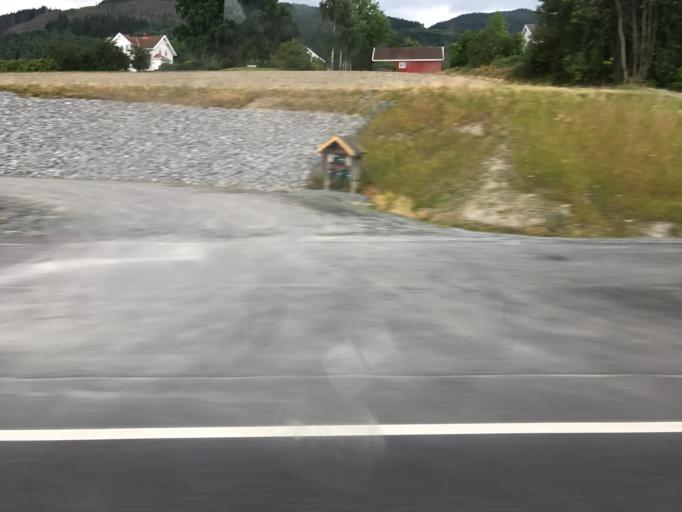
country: NO
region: Oppland
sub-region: Ostre Toten
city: Skreia
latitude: 60.6385
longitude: 11.0694
